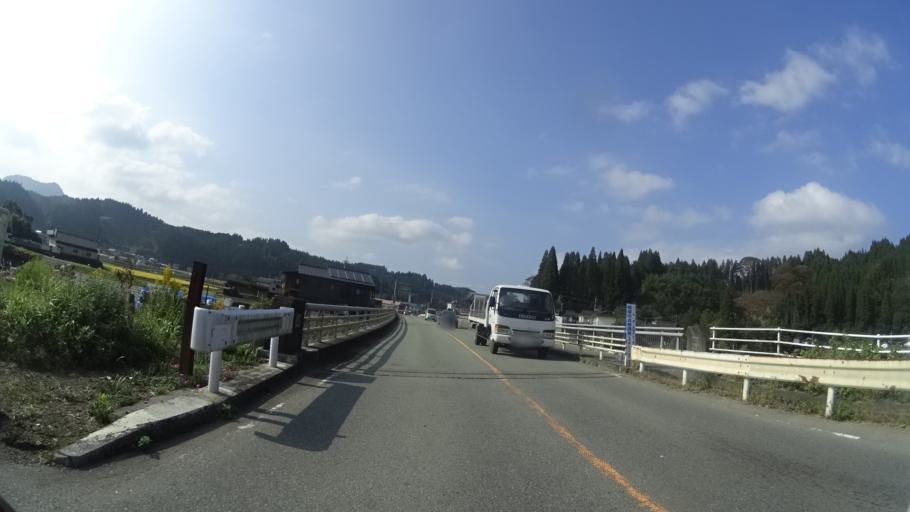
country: JP
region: Kumamoto
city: Aso
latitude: 33.1068
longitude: 131.0663
